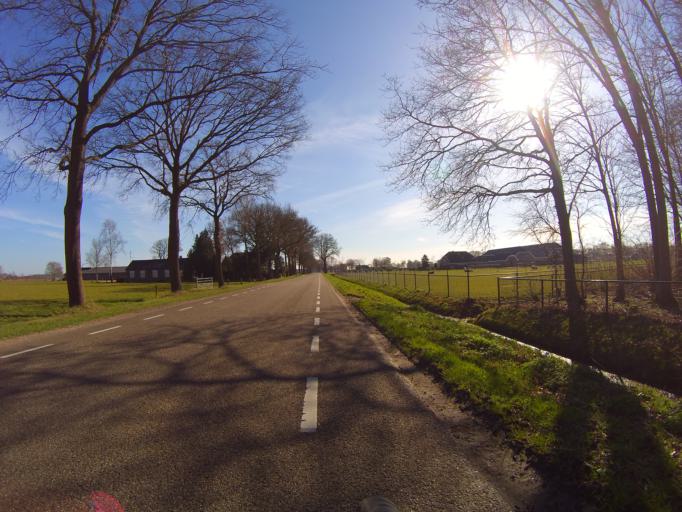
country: NL
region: Utrecht
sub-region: Gemeente Utrechtse Heuvelrug
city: Overberg
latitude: 52.0638
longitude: 5.4995
